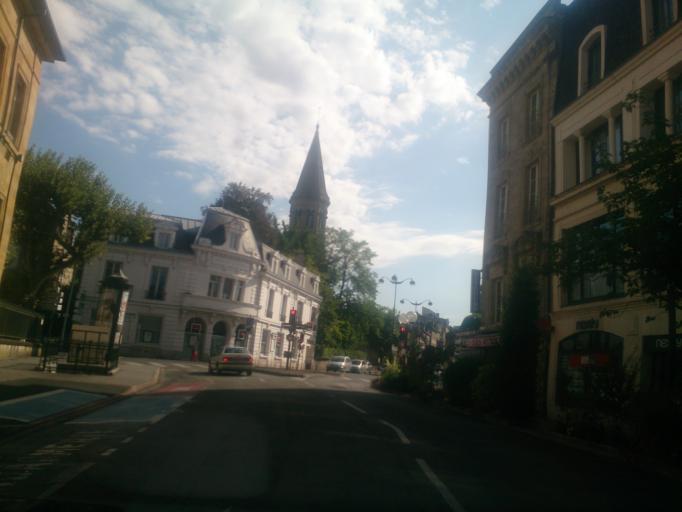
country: FR
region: Limousin
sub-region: Departement de la Correze
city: Brive-la-Gaillarde
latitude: 45.1571
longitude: 1.5318
